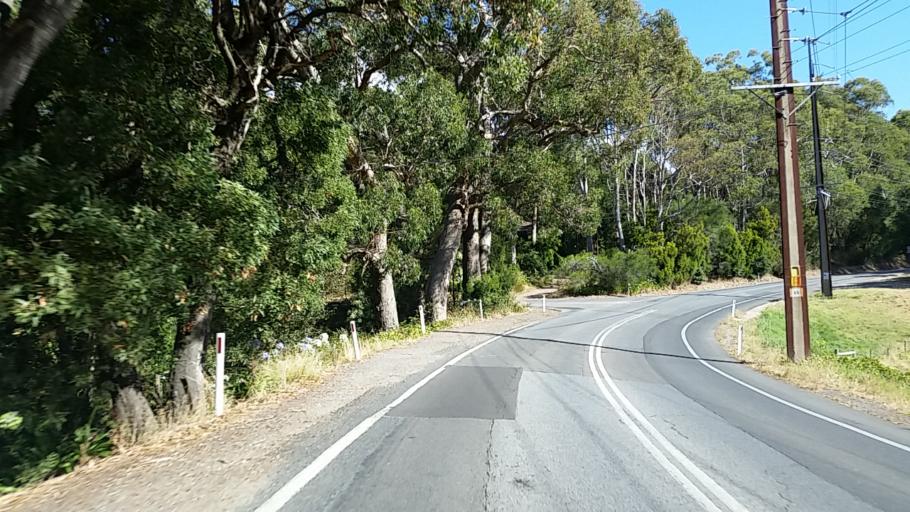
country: AU
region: South Australia
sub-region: Adelaide Hills
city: Bridgewater
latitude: -34.9852
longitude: 138.7265
